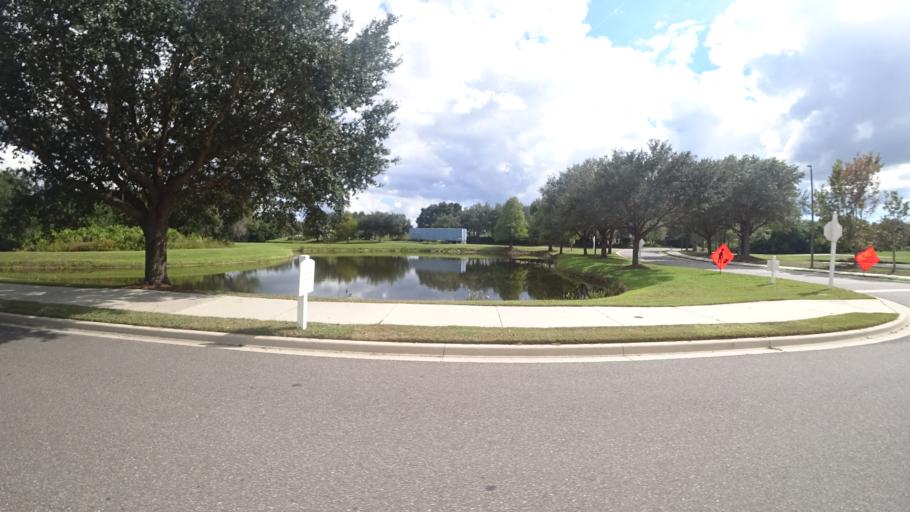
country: US
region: Florida
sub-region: Sarasota County
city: The Meadows
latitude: 27.3950
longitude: -82.4016
